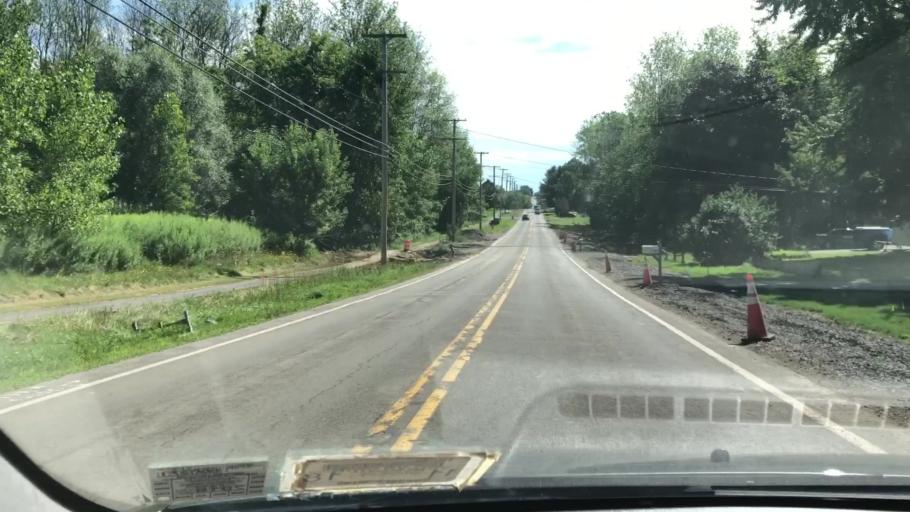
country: US
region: New York
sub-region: Monroe County
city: Fairport
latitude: 43.1084
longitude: -77.4132
